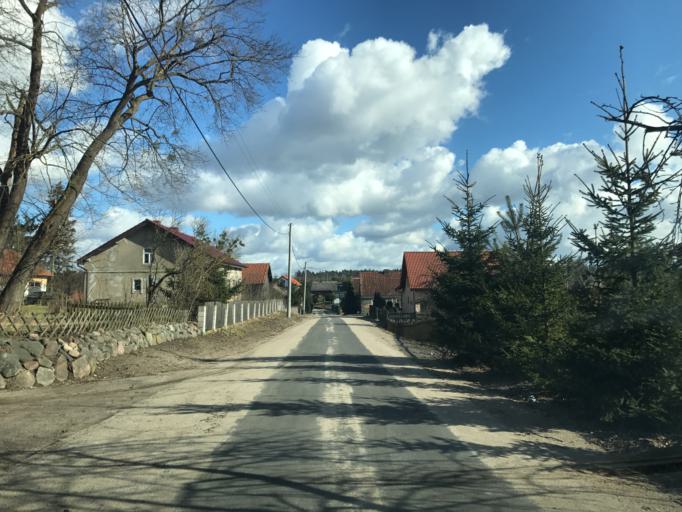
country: PL
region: Warmian-Masurian Voivodeship
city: Dobre Miasto
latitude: 54.0268
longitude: 20.4063
